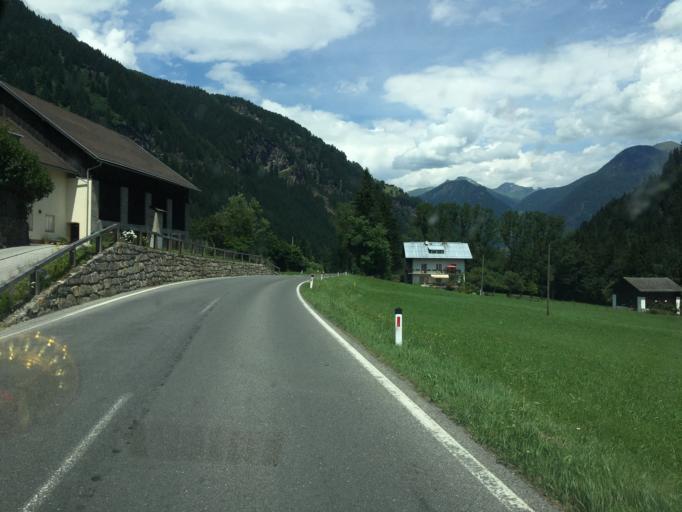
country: AT
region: Carinthia
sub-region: Politischer Bezirk Spittal an der Drau
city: Winklern
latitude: 46.8743
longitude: 12.8799
